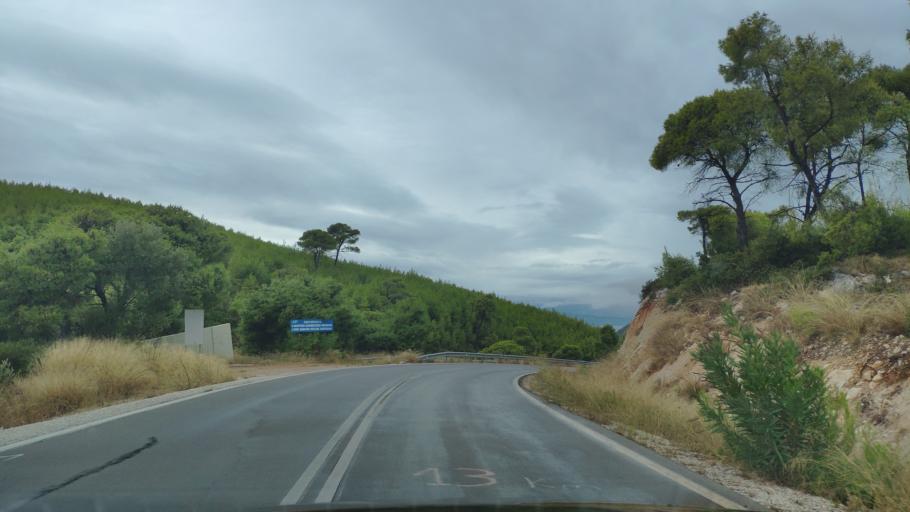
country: GR
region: Peloponnese
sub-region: Nomos Korinthias
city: Perachora
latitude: 38.0292
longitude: 22.9319
